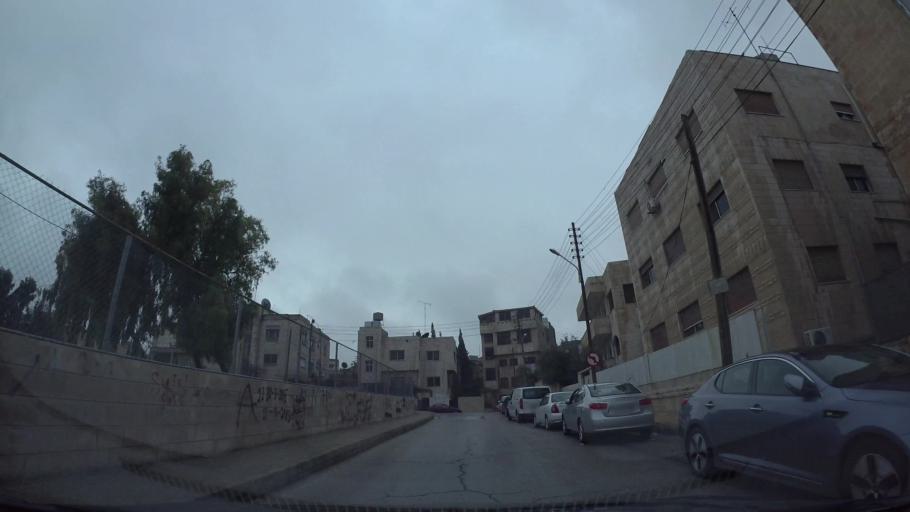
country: JO
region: Amman
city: Amman
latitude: 31.9615
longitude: 35.9308
